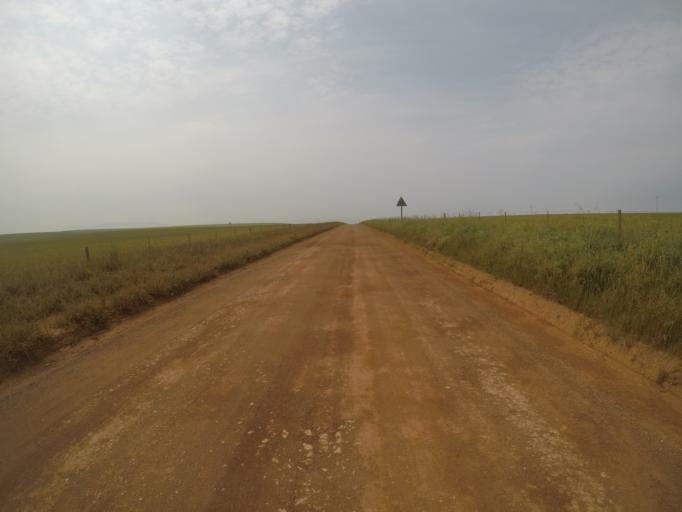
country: ZA
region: Western Cape
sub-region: City of Cape Town
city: Kraaifontein
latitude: -33.7259
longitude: 18.6436
